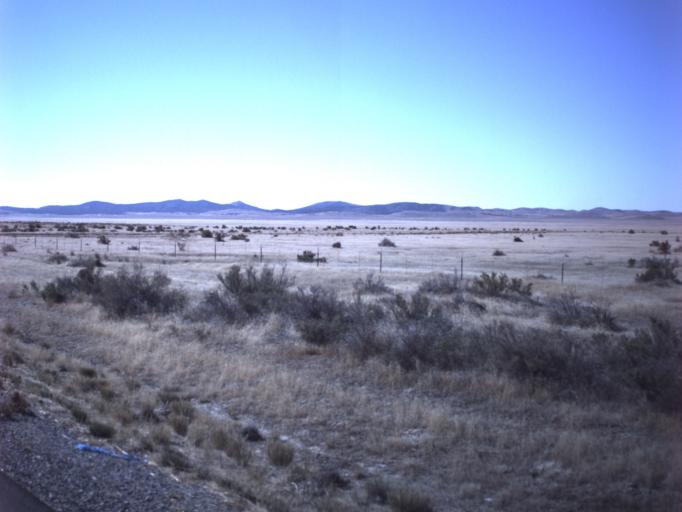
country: US
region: Utah
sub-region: Tooele County
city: Grantsville
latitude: 40.3334
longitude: -112.7445
